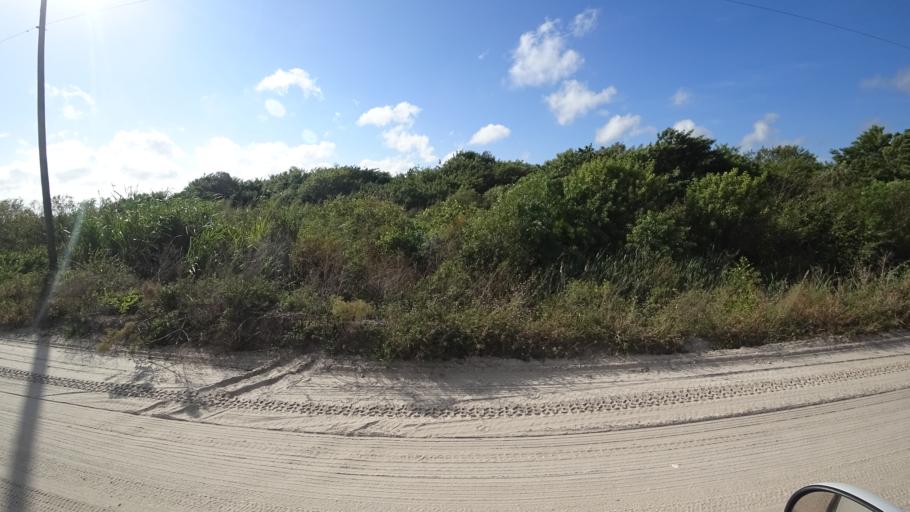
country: US
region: Florida
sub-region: Hillsborough County
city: Wimauma
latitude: 27.5421
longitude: -82.3214
